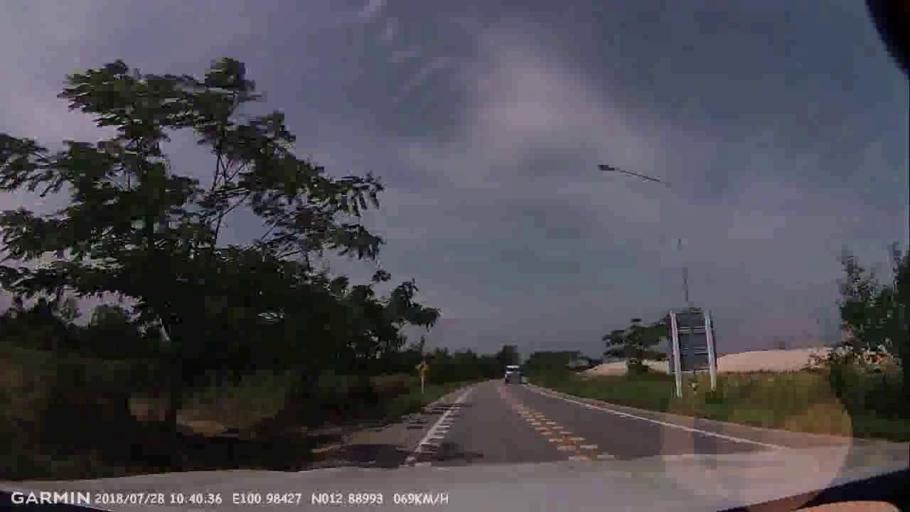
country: TH
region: Chon Buri
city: Phatthaya
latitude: 12.8898
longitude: 100.9842
